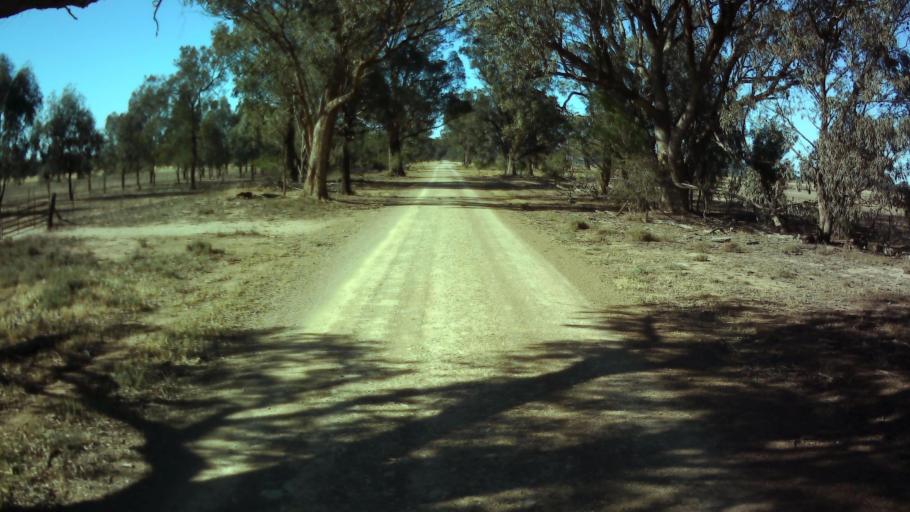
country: AU
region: New South Wales
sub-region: Weddin
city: Grenfell
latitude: -33.9296
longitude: 147.8731
